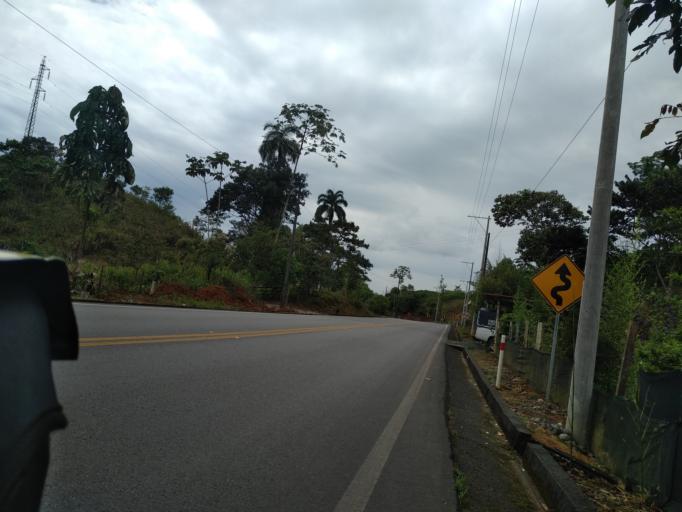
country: EC
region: Pastaza
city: Puyo
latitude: -1.3378
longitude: -77.9178
